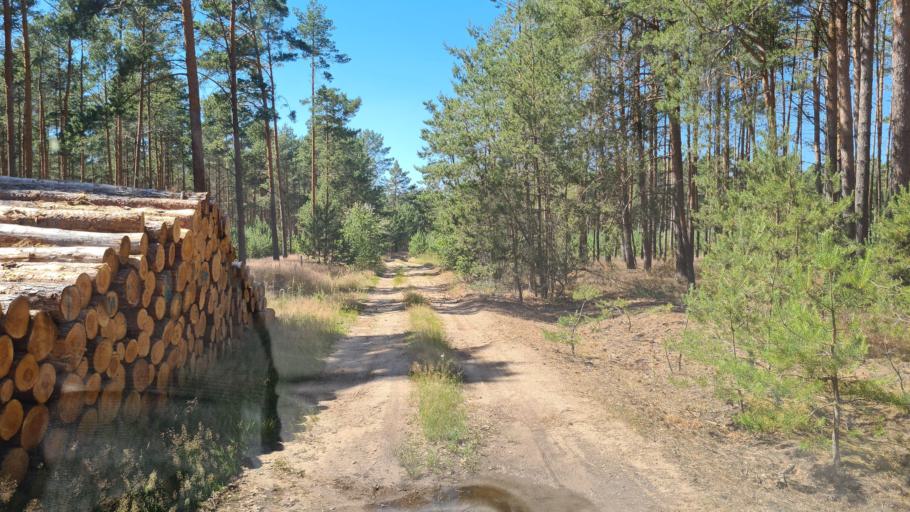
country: DE
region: Brandenburg
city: Treuenbrietzen
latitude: 52.0529
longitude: 12.8042
